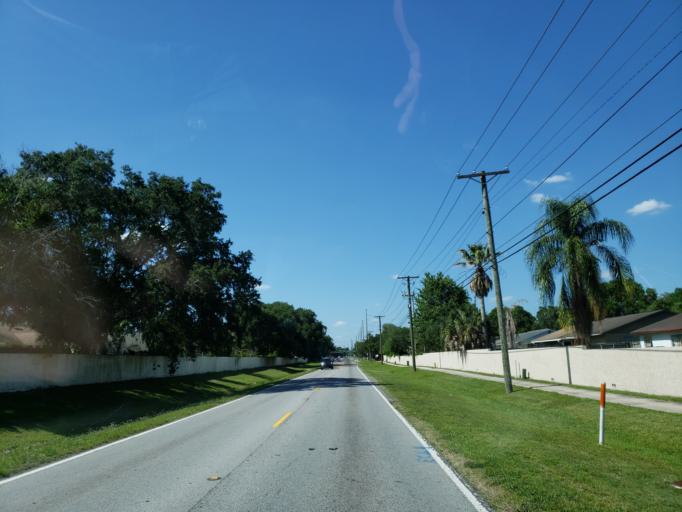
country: US
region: Florida
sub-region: Hillsborough County
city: Mango
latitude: 27.9720
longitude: -82.3104
